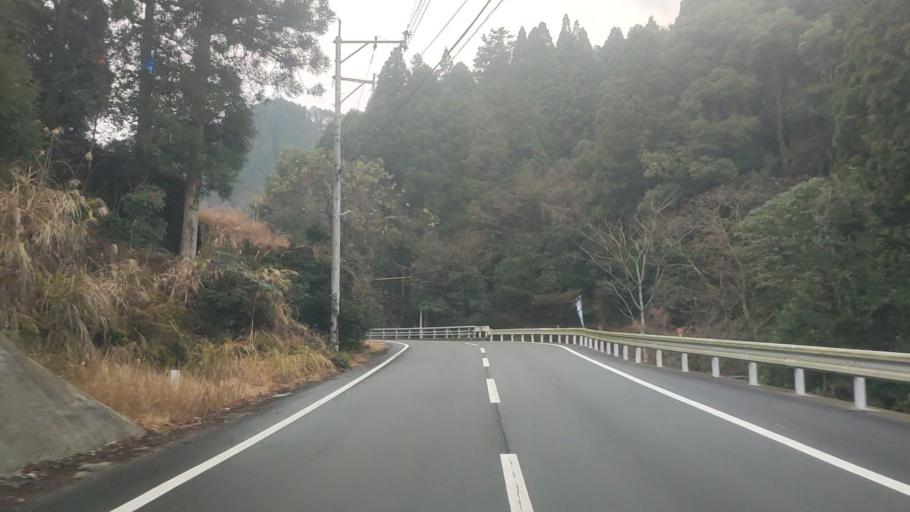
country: JP
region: Kumamoto
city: Matsubase
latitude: 32.5921
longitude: 130.8872
